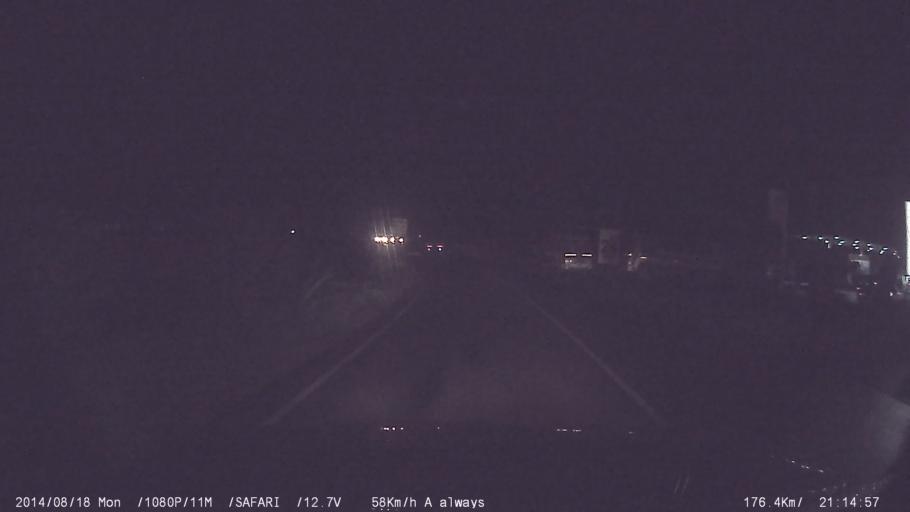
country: IN
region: Kerala
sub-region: Thrissur District
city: Trichur
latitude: 10.5545
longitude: 76.3176
